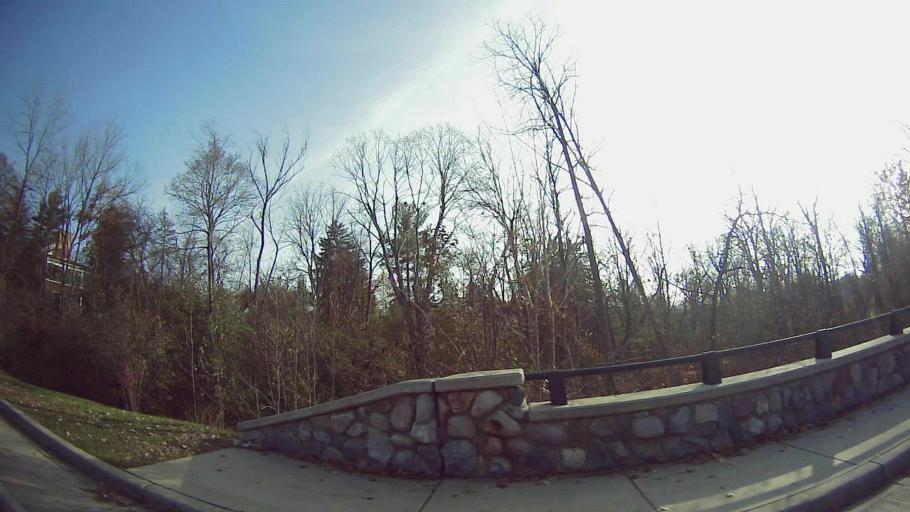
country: US
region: Michigan
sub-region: Oakland County
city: Beverly Hills
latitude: 42.5384
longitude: -83.2281
